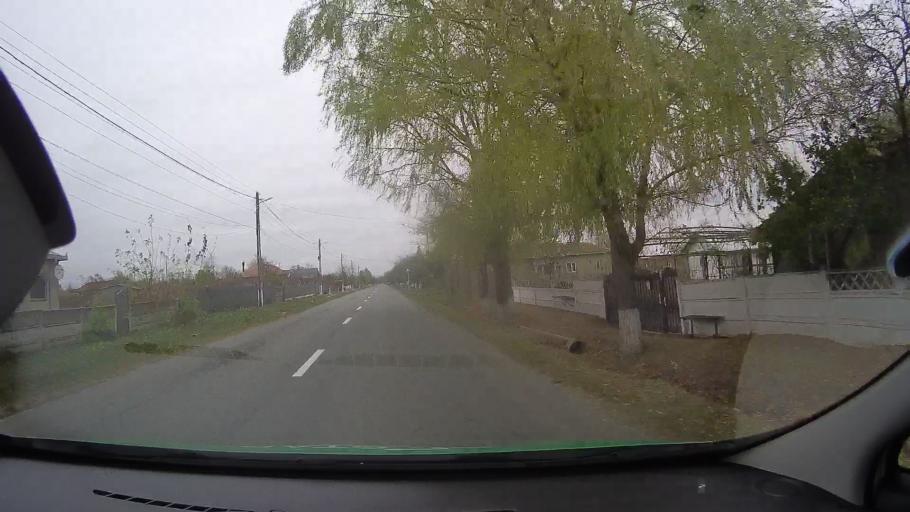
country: RO
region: Constanta
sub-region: Comuna Silistea
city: Silistea
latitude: 44.4420
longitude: 28.2329
